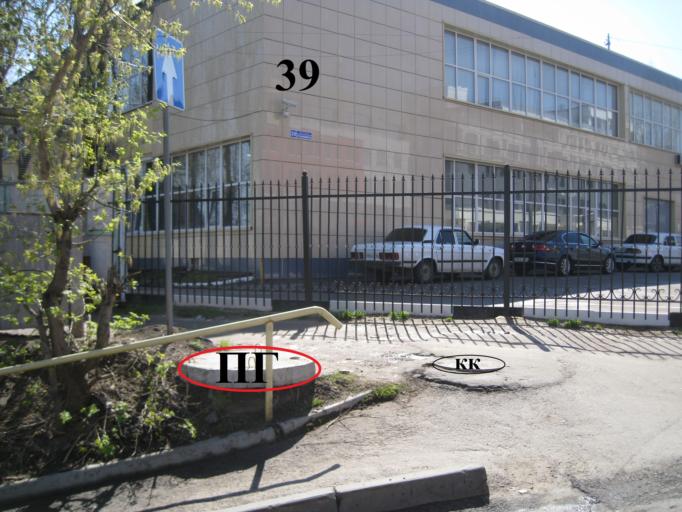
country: RU
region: Voronezj
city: Voronezh
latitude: 51.6552
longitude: 39.1950
